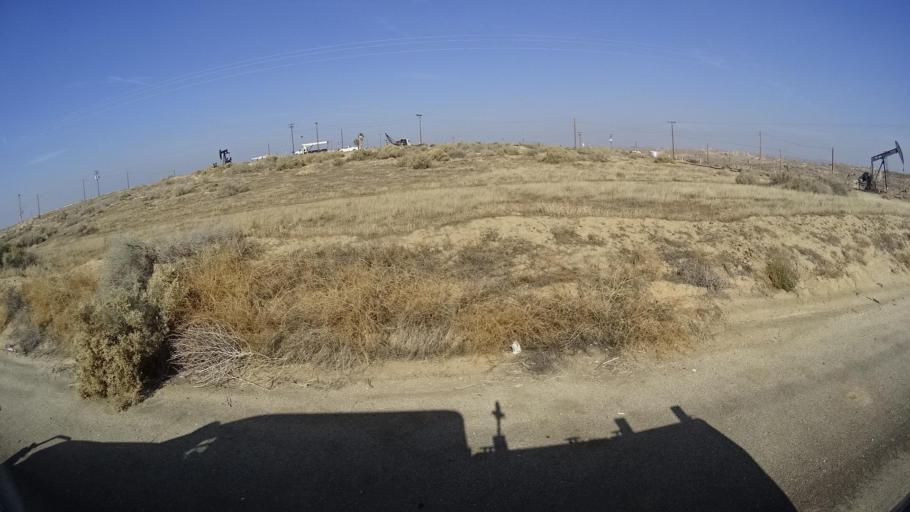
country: US
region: California
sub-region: Kern County
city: Oildale
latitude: 35.5299
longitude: -119.0896
